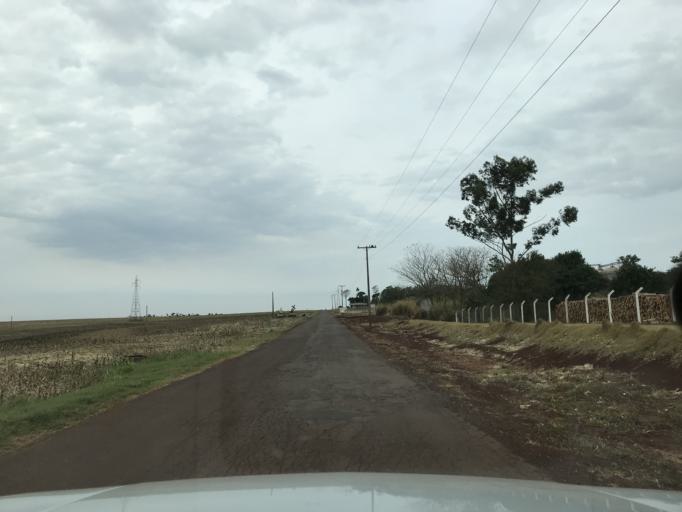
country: BR
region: Parana
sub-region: Palotina
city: Palotina
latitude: -24.2848
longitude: -53.7960
